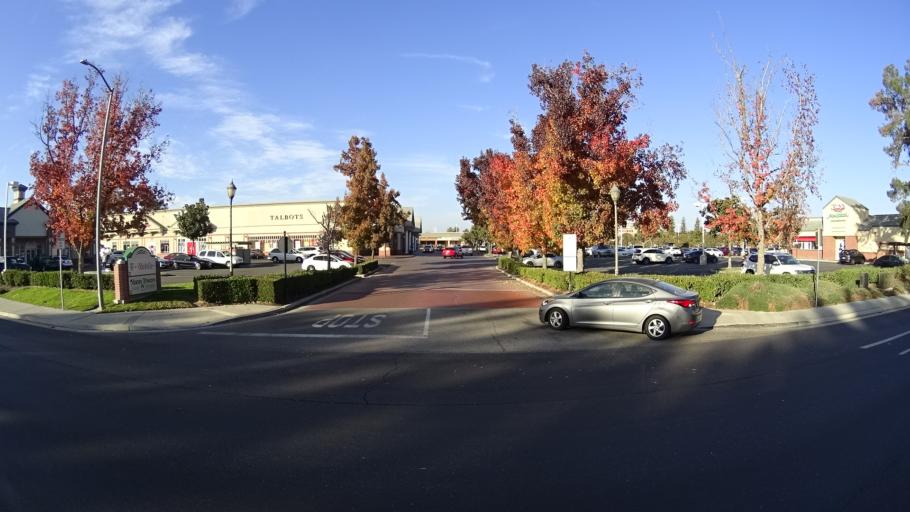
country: US
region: California
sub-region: Kern County
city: Greenacres
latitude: 35.3399
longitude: -119.1052
